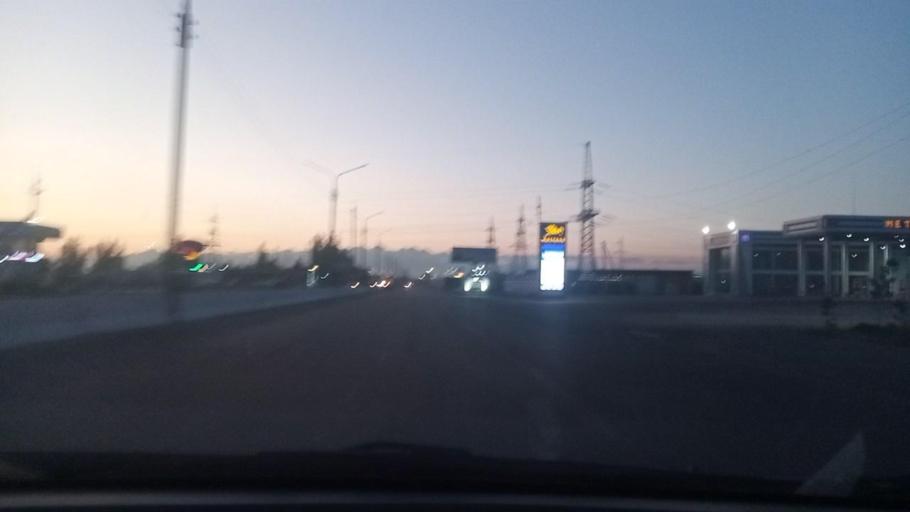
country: UZ
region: Toshkent Shahri
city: Tashkent
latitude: 41.2440
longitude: 69.2290
